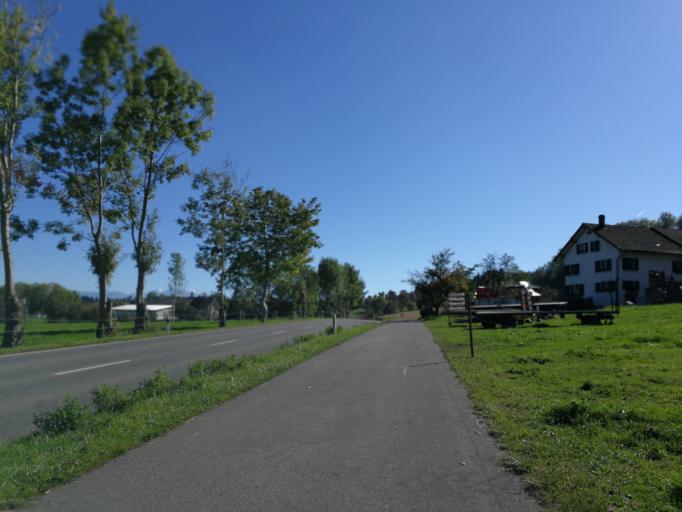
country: CH
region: Zurich
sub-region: Bezirk Uster
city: Egg
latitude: 47.2937
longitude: 8.6913
